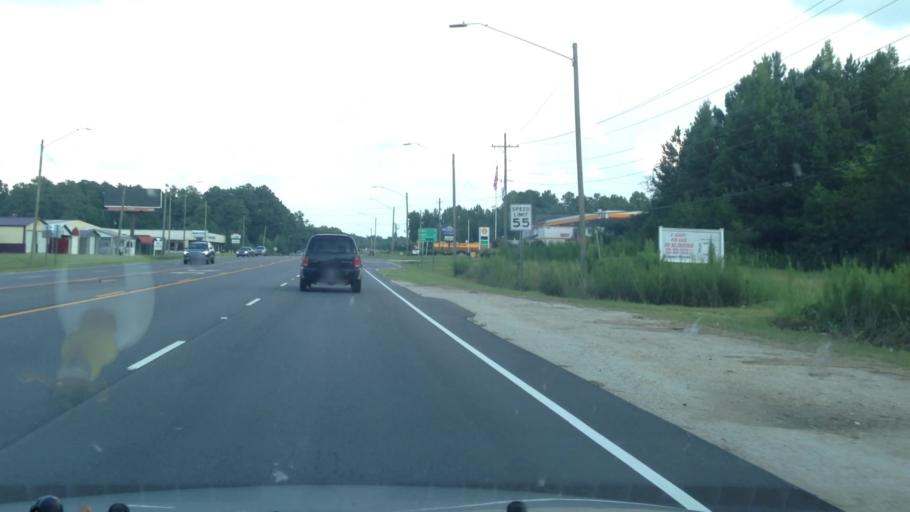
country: US
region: North Carolina
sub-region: Harnett County
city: Lillington
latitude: 35.4168
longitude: -78.8012
